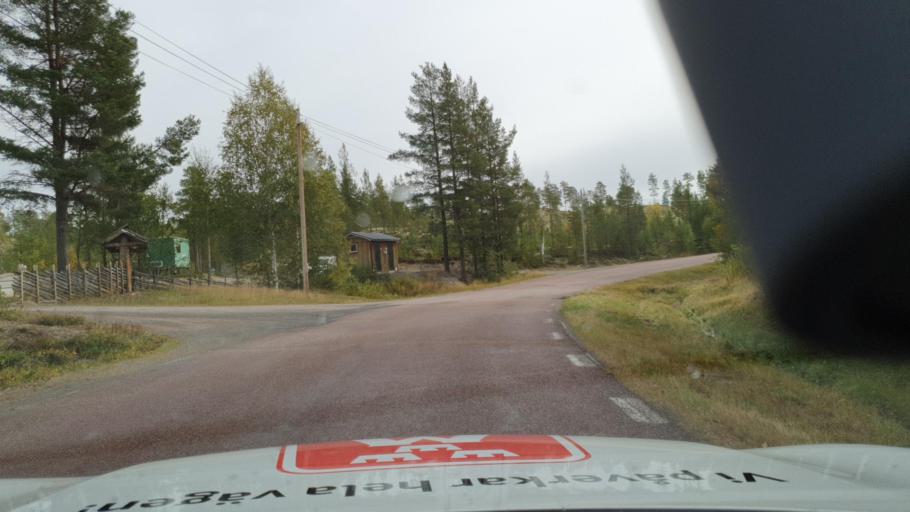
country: NO
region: Hedmark
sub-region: Trysil
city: Innbygda
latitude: 61.8728
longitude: 12.6986
